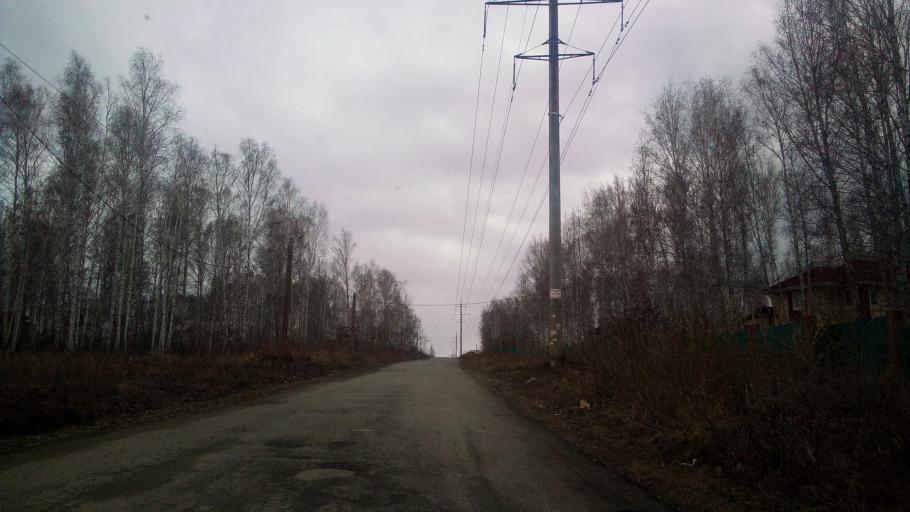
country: RU
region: Chelyabinsk
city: Sargazy
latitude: 55.1330
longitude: 61.2449
